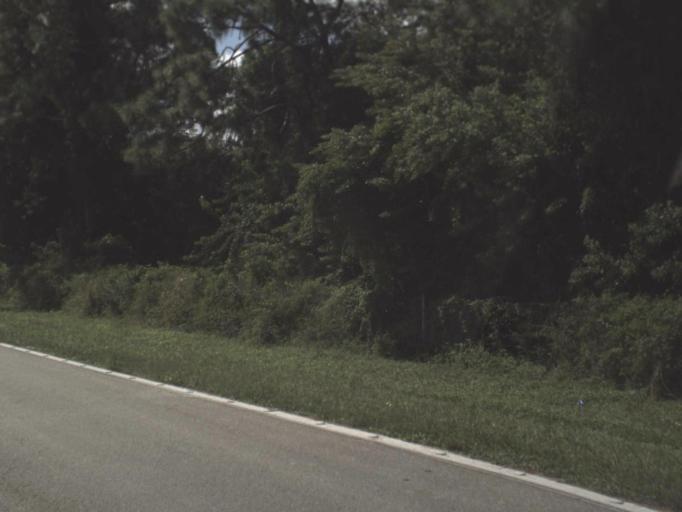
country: US
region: Florida
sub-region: Hendry County
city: LaBelle
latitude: 26.7280
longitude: -81.4377
